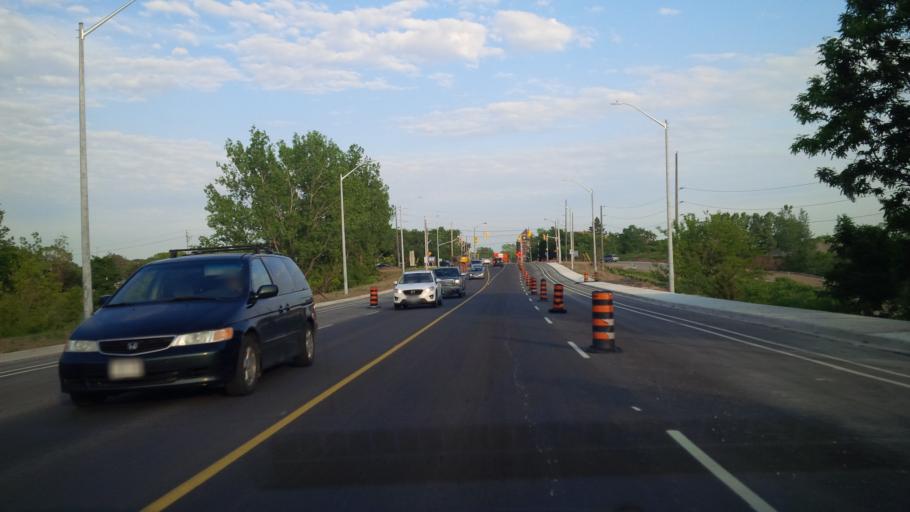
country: CA
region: Ontario
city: Hamilton
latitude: 43.3103
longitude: -79.8573
